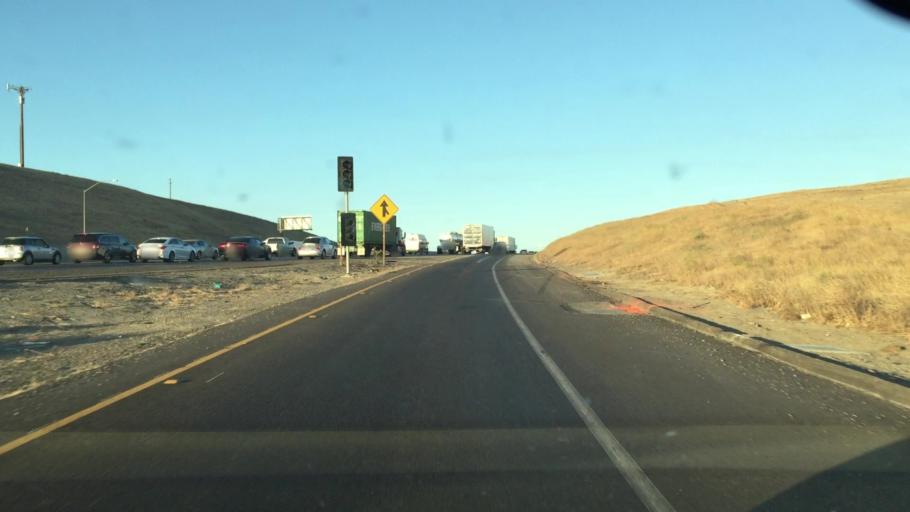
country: US
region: California
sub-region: San Joaquin County
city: Mountain House
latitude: 37.7406
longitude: -121.5833
